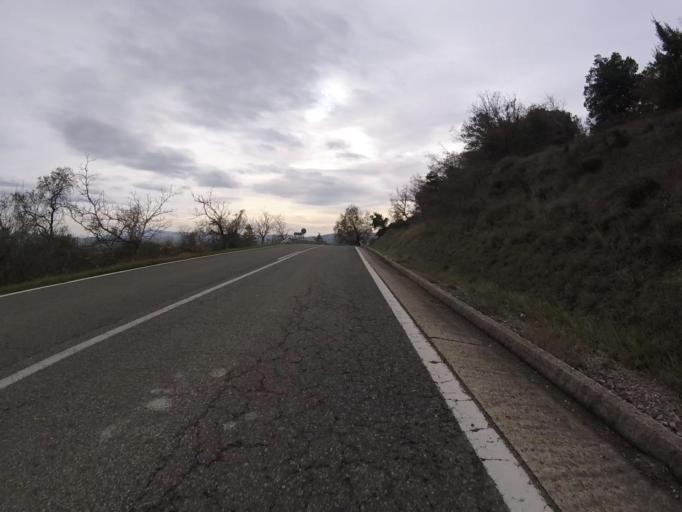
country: ES
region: Navarre
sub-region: Provincia de Navarra
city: Lezaun
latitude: 42.7338
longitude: -2.0148
